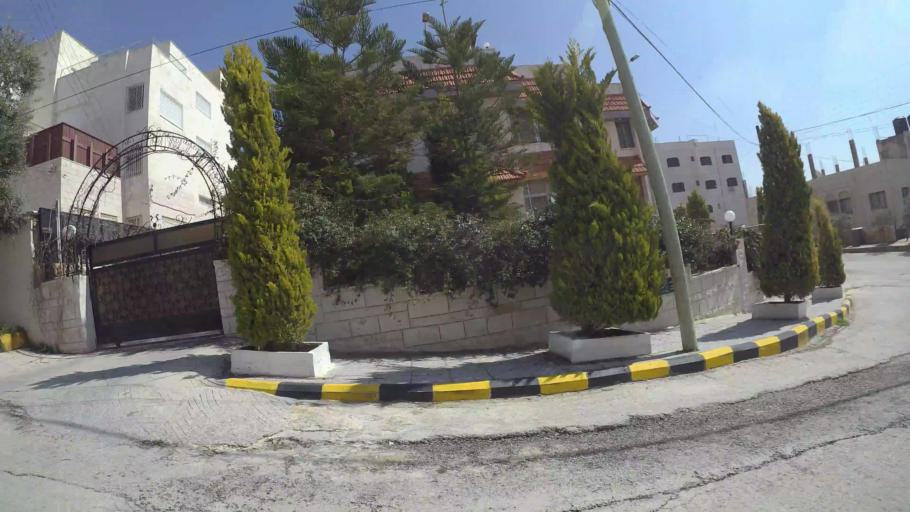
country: JO
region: Amman
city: Al Bunayyat ash Shamaliyah
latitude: 31.8850
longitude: 35.8958
